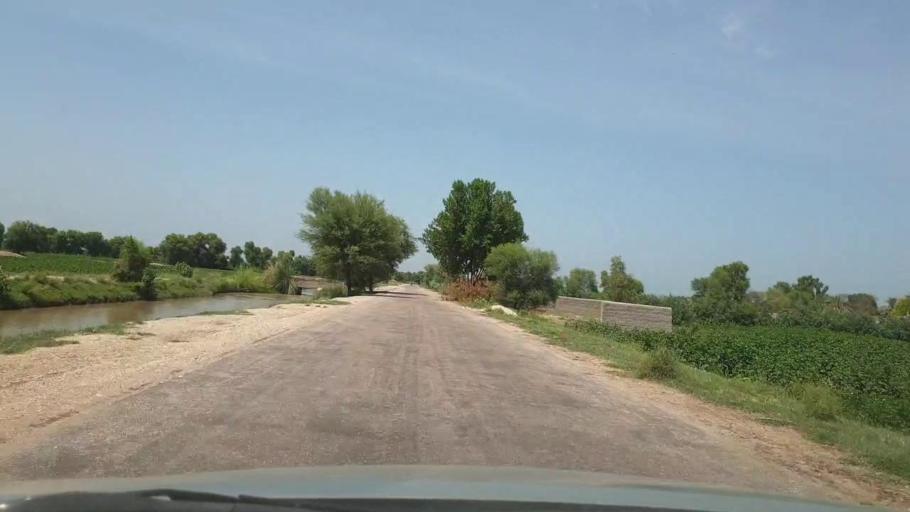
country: PK
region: Sindh
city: Pano Aqil
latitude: 27.6847
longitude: 69.1103
